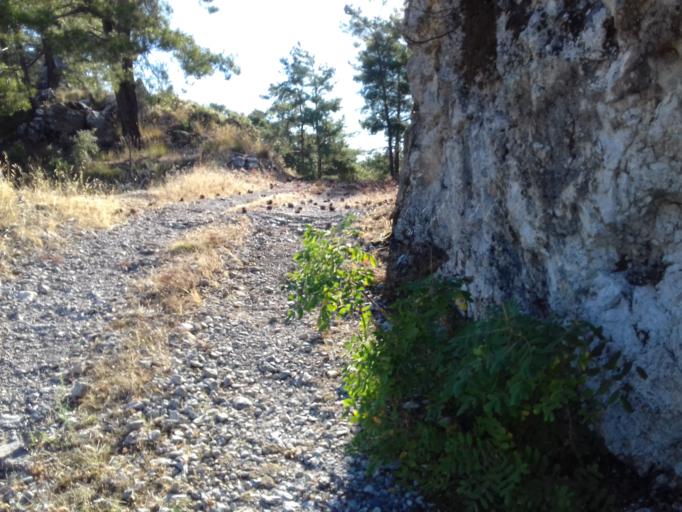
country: TR
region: Mugla
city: Yaniklar
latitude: 36.7932
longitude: 29.0268
